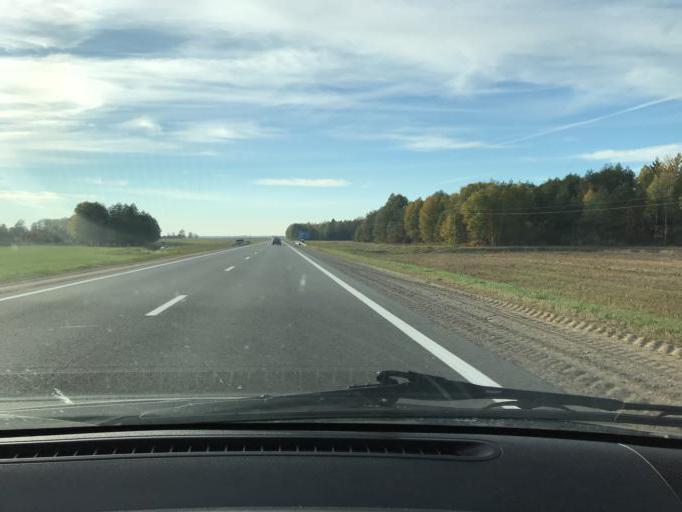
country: BY
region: Brest
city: Ivanava
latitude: 52.1563
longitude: 25.7119
